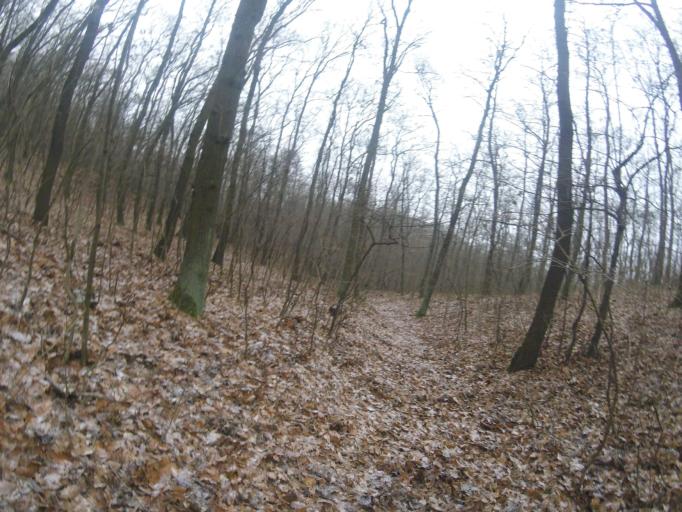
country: HU
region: Fejer
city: Bicske
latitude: 47.4176
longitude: 18.5790
